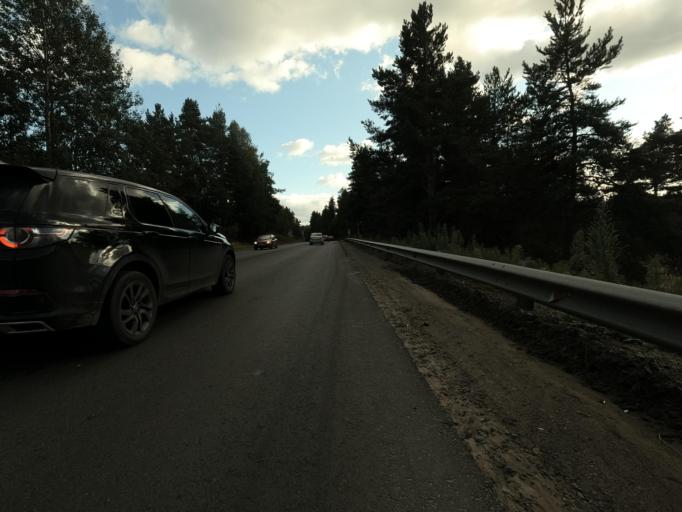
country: RU
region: Leningrad
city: Koltushi
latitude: 59.9623
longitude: 30.6584
